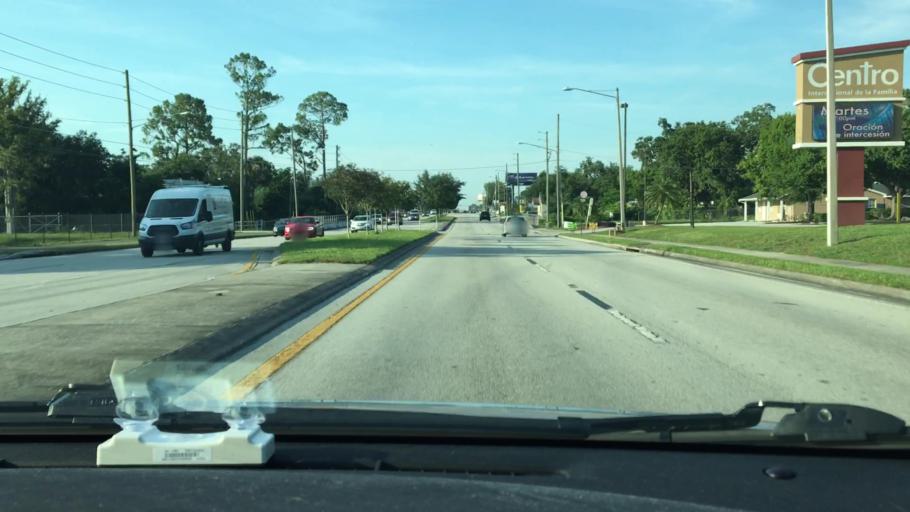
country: US
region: Florida
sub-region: Orange County
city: Union Park
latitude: 28.5749
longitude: -81.2862
